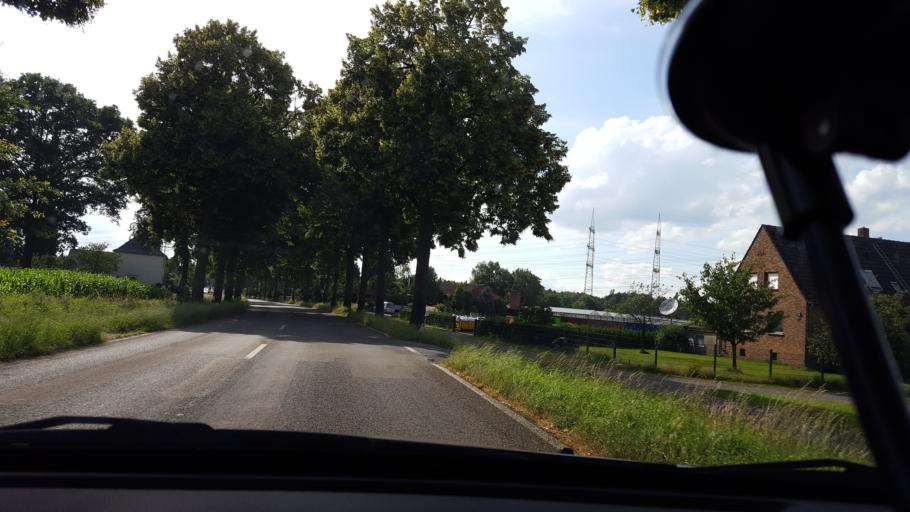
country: DE
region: North Rhine-Westphalia
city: Marl
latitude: 51.6578
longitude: 7.0625
